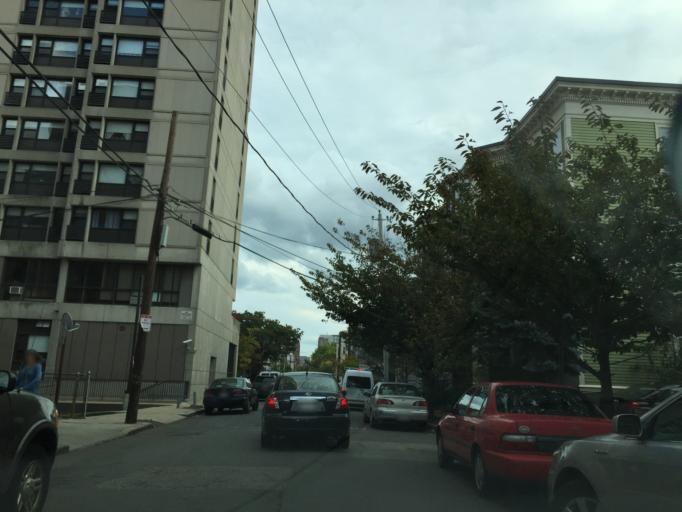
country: US
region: Massachusetts
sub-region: Middlesex County
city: Cambridge
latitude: 42.3643
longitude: -71.1048
